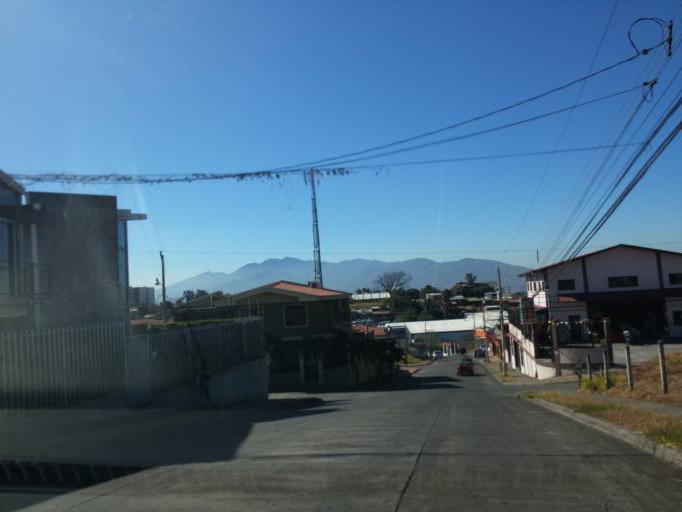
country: CR
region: Alajuela
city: Alajuela
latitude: 10.0196
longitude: -84.2246
